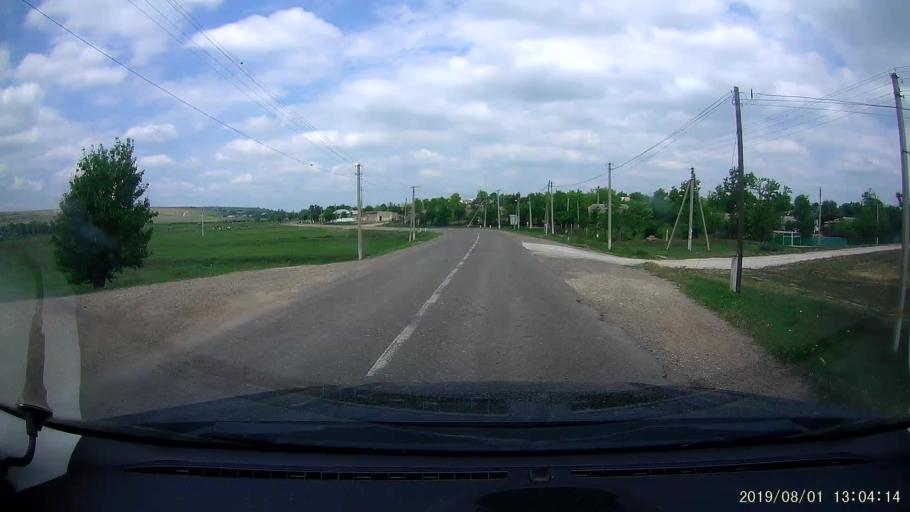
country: MD
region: Gagauzia
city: Vulcanesti
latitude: 45.7659
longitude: 28.3818
